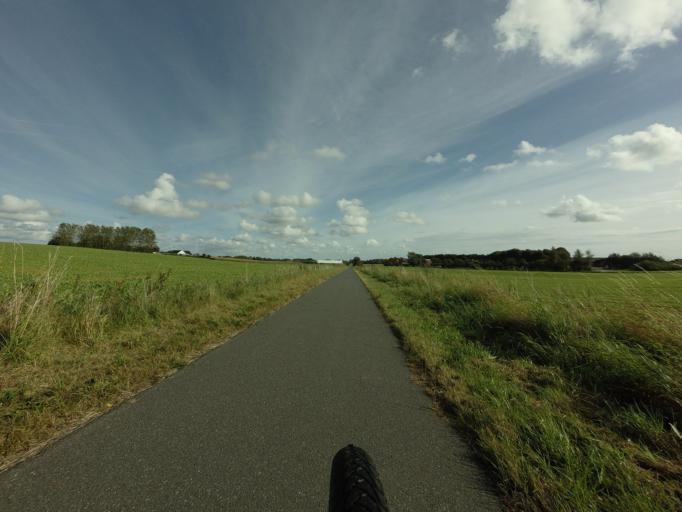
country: DK
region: Central Jutland
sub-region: Viborg Kommune
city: Bjerringbro
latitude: 56.4938
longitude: 9.6676
